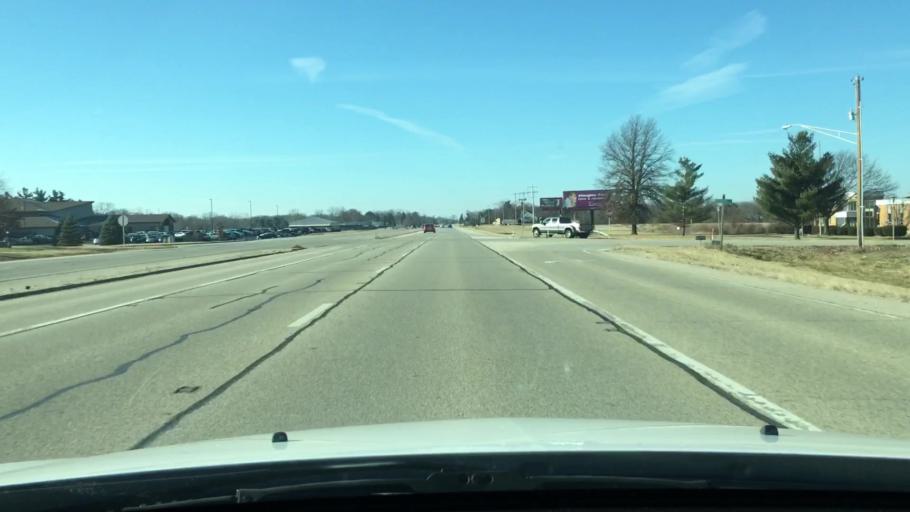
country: US
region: Illinois
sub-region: Woodford County
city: Germantown Hills
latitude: 40.7719
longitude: -89.4415
